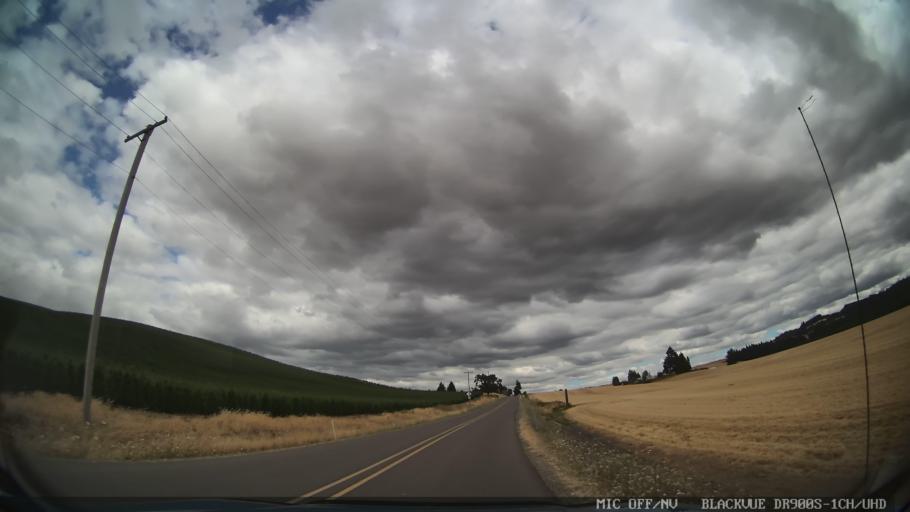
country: US
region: Oregon
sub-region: Marion County
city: Sublimity
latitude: 44.8724
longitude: -122.7332
